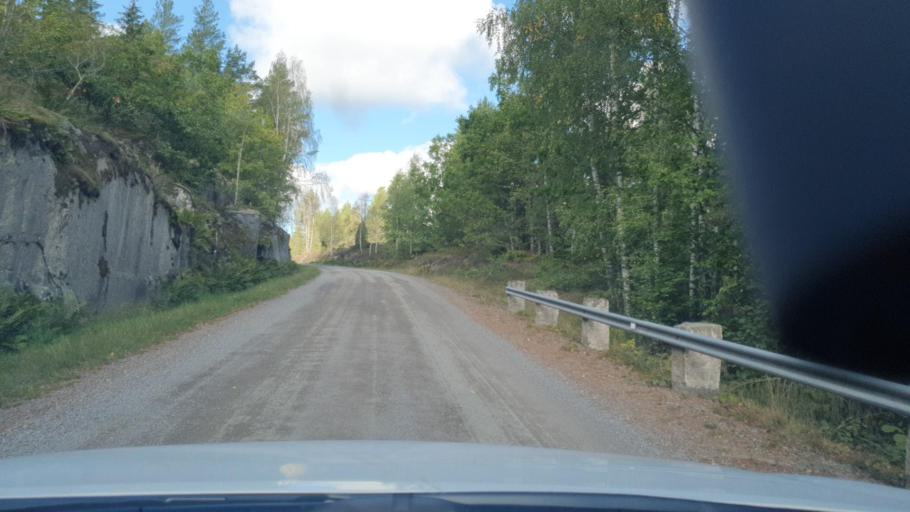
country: SE
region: Kalmar
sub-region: Vasterviks Kommun
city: Ankarsrum
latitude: 57.6949
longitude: 16.4650
